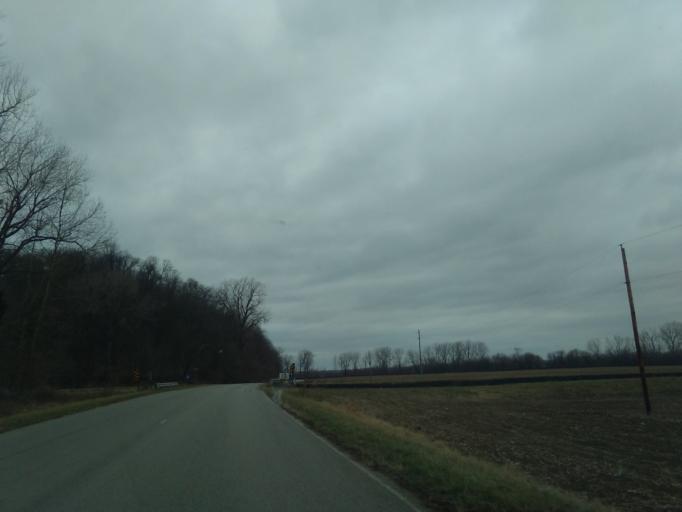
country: US
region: Missouri
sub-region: Holt County
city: Mound City
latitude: 40.0259
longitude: -95.3664
